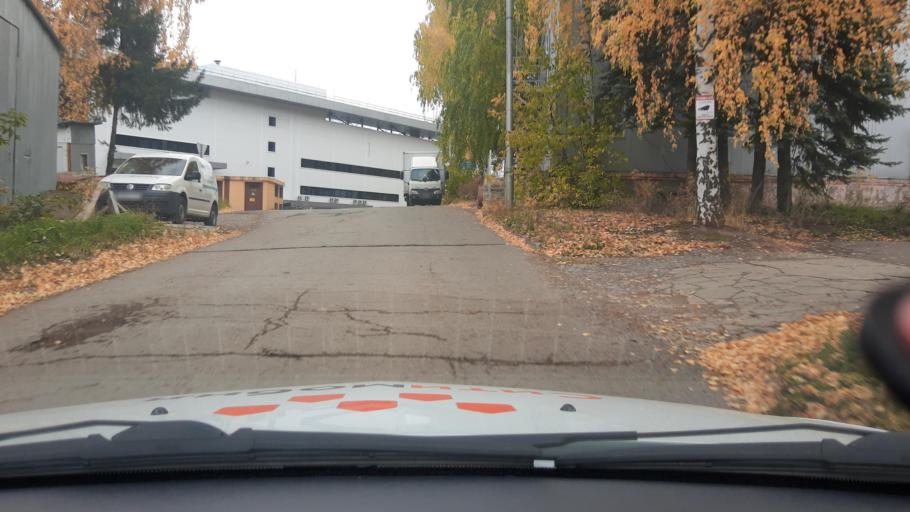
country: RU
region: Bashkortostan
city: Ufa
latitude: 54.7237
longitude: 56.0180
